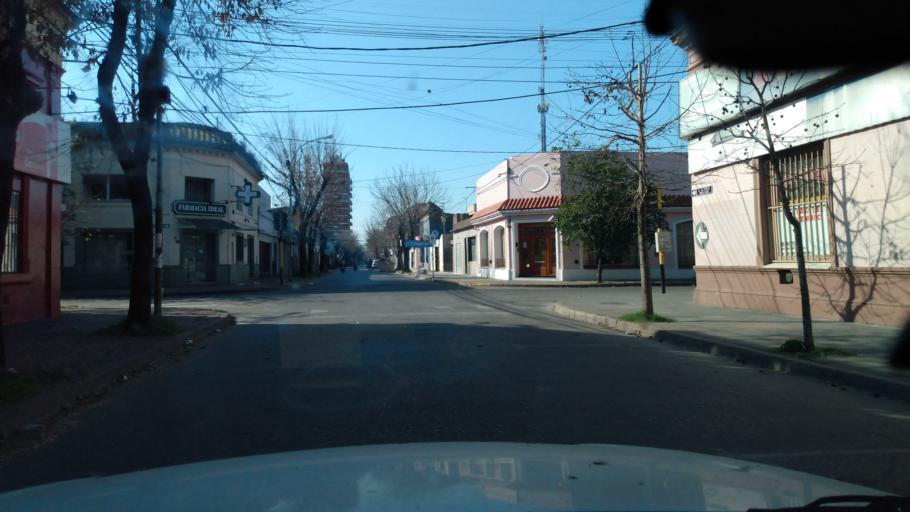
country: AR
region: Buenos Aires
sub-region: Partido de Lujan
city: Lujan
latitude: -34.5679
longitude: -59.1132
